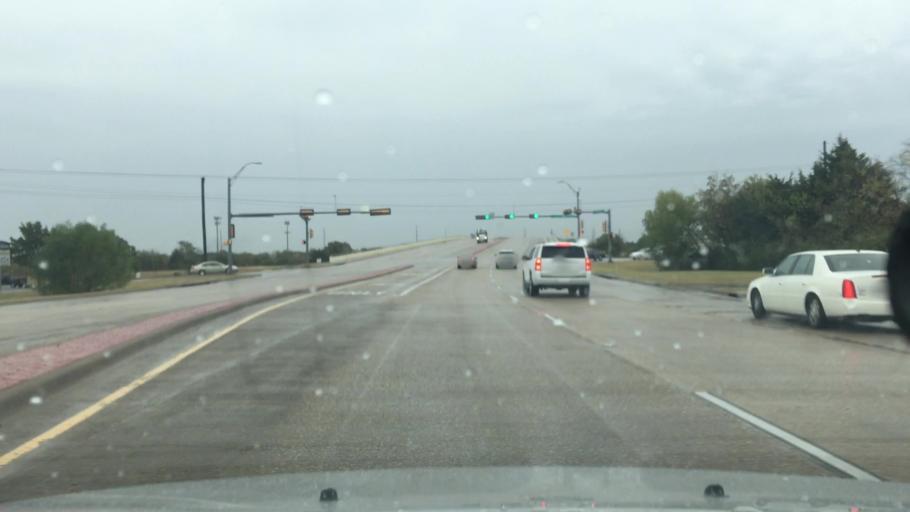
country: US
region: Texas
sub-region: Denton County
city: Denton
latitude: 33.2355
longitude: -97.0999
